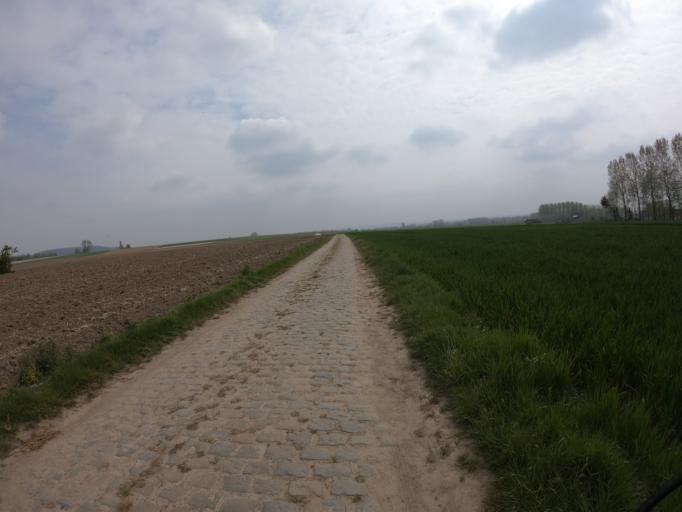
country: BE
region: Flanders
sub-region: Provincie Oost-Vlaanderen
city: Ronse
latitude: 50.7448
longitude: 3.5336
